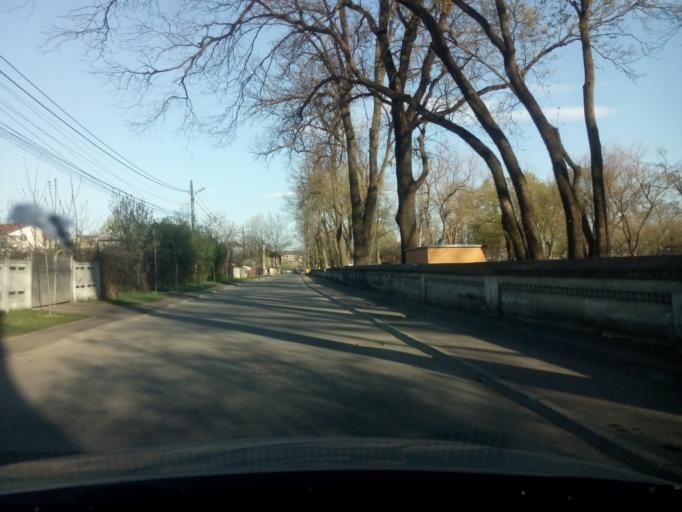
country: RO
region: Ilfov
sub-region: Comuna Mogosoaia
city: Mogosoaia
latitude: 44.5253
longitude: 26.0019
